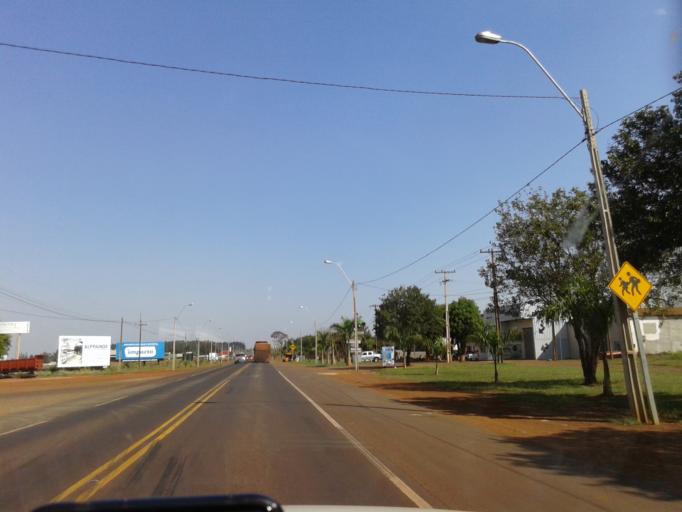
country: PY
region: Alto Parana
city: Santa Rita
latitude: -25.7530
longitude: -55.0579
